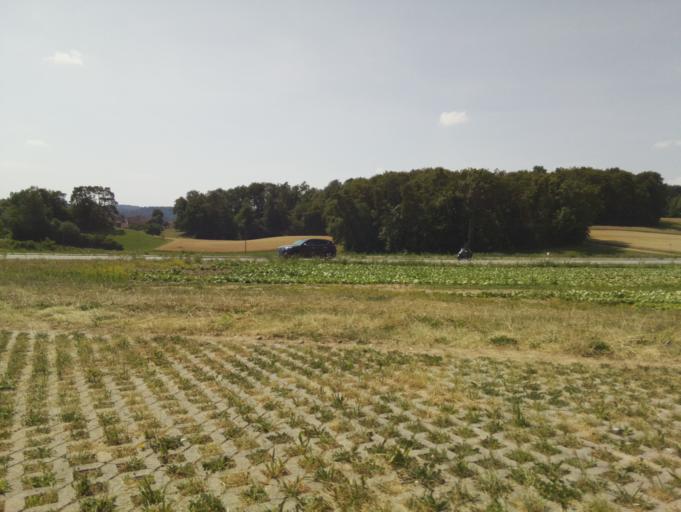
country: CH
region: Zurich
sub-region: Bezirk Andelfingen
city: Kleinandelfingen
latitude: 47.6106
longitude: 8.7117
